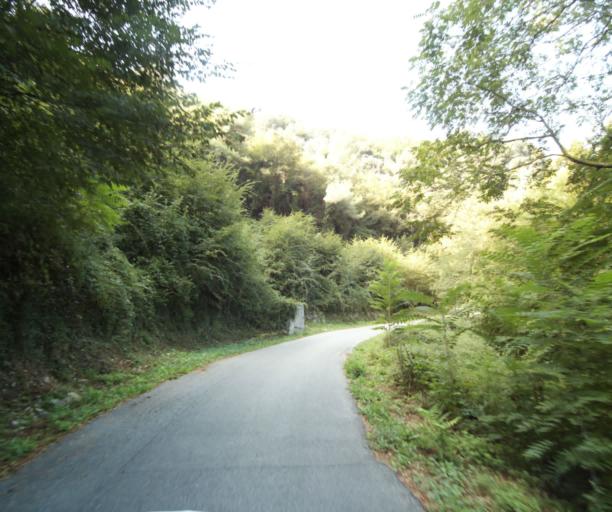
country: FR
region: Provence-Alpes-Cote d'Azur
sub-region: Departement des Alpes-Maritimes
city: Drap
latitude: 43.7608
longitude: 7.3487
